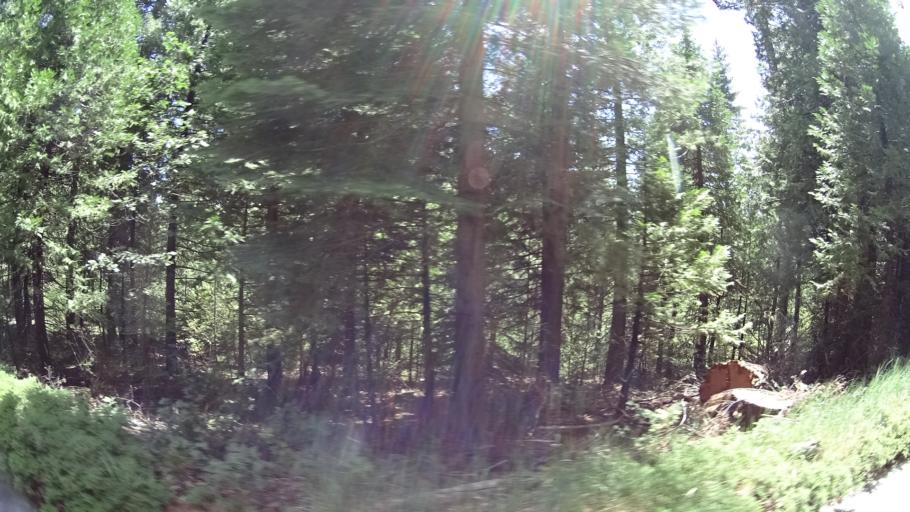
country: US
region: California
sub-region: Calaveras County
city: Arnold
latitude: 38.2973
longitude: -120.2543
